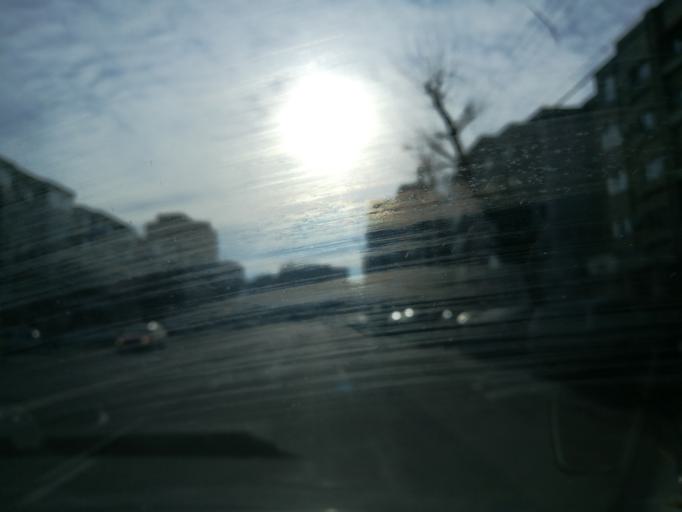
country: RO
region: Constanta
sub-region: Municipiul Constanta
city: Constanta
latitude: 44.1746
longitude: 28.6118
